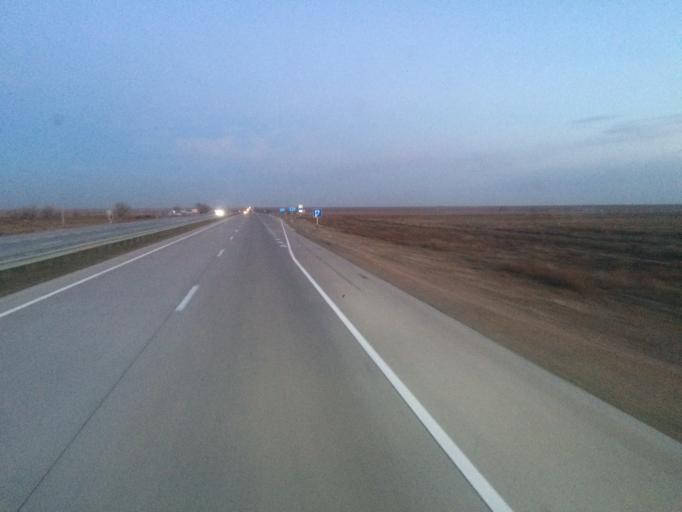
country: KZ
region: Ongtustik Qazaqstan
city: Temirlanovka
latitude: 42.8473
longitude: 69.0906
